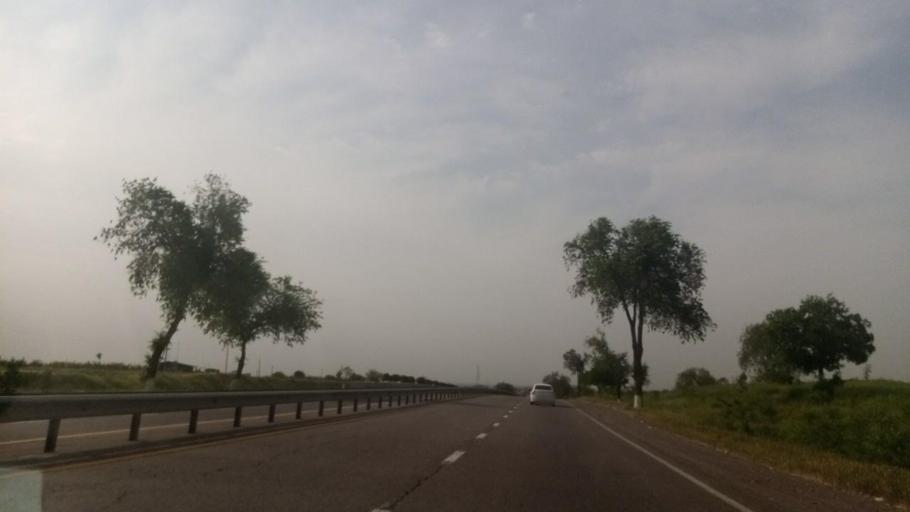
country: UZ
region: Toshkent
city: Tuytepa
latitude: 41.1077
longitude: 69.4510
